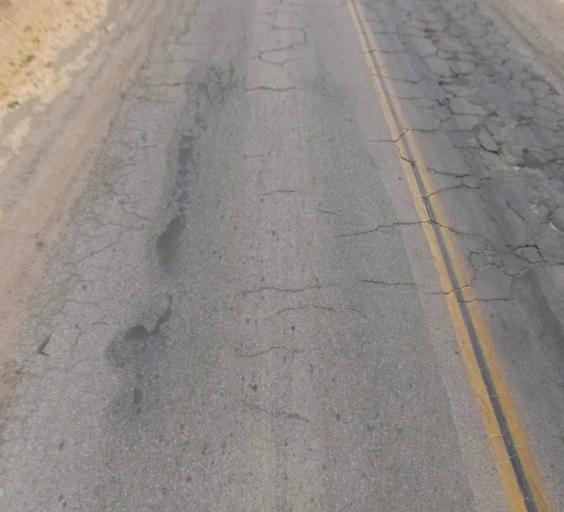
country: US
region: California
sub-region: Madera County
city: Parksdale
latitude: 36.9744
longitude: -120.0284
